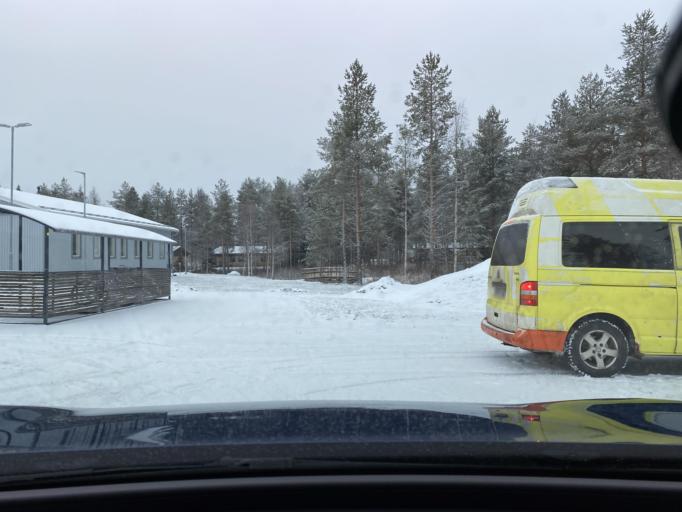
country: FI
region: Lapland
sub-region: Rovaniemi
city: Ranua
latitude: 65.9249
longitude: 26.5167
